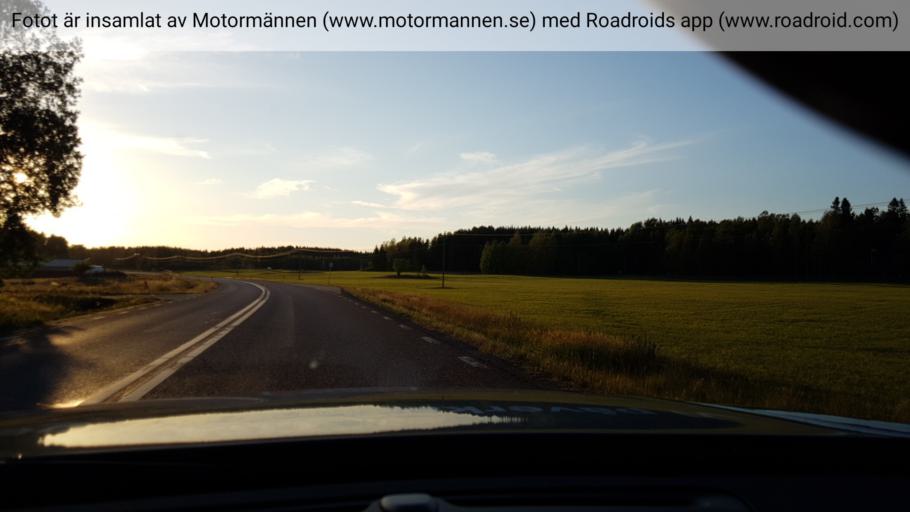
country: SE
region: OErebro
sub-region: Karlskoga Kommun
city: Karlskoga
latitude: 59.3902
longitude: 14.4695
